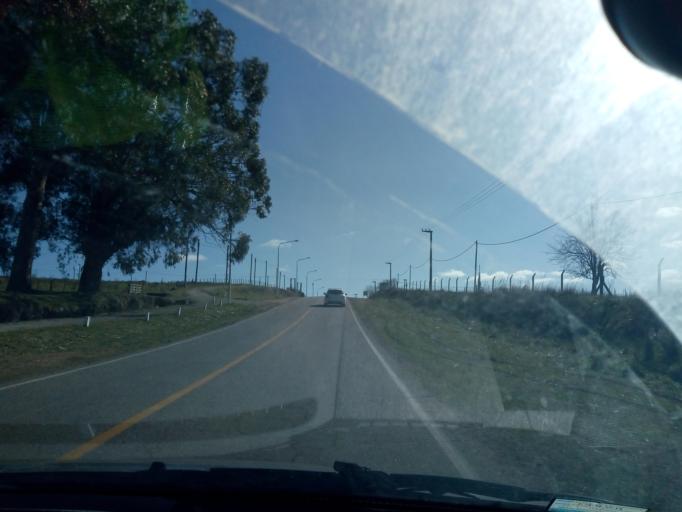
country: AR
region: Buenos Aires
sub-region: Partido de Tandil
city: Tandil
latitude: -37.3540
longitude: -59.1482
